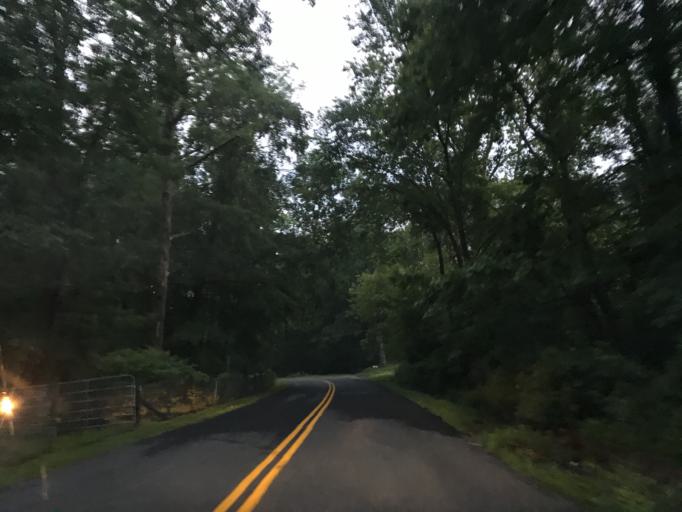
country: US
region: Maryland
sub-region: Harford County
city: Fallston
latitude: 39.4936
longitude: -76.4183
